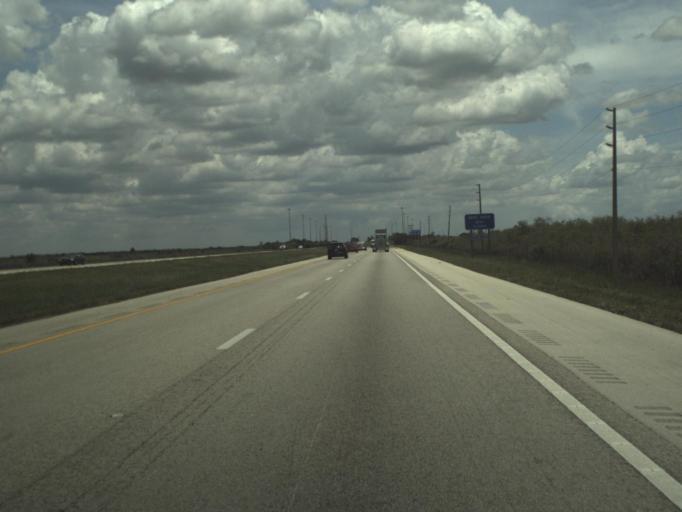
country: US
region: Florida
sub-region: Broward County
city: Weston
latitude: 26.1462
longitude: -80.6503
